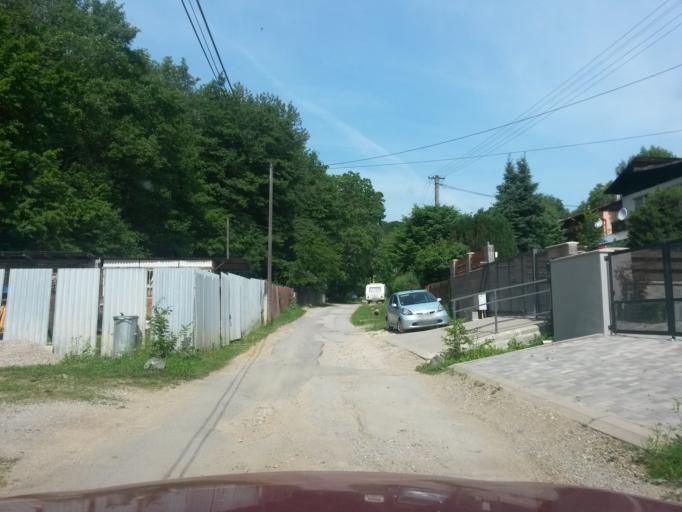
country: SK
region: Kosicky
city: Kosice
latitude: 48.7312
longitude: 21.1307
